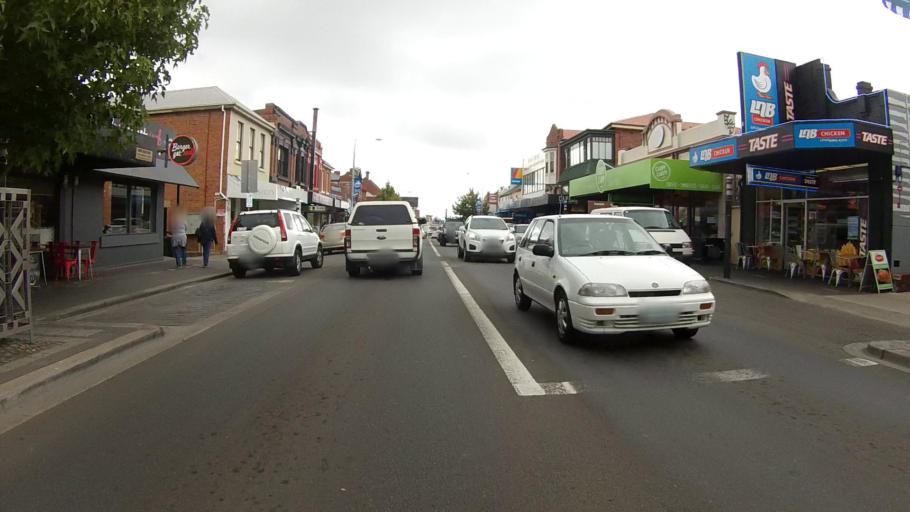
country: AU
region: Tasmania
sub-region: Hobart
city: Hobart
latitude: -42.8736
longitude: 147.3160
